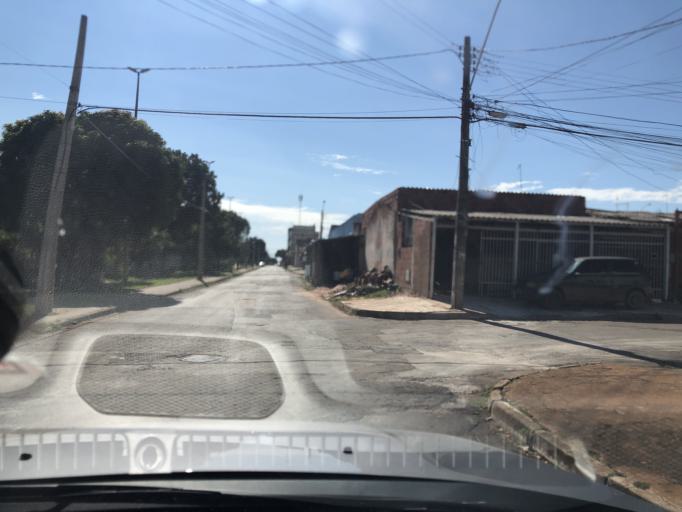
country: BR
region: Federal District
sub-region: Brasilia
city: Brasilia
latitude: -15.7927
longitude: -48.1255
